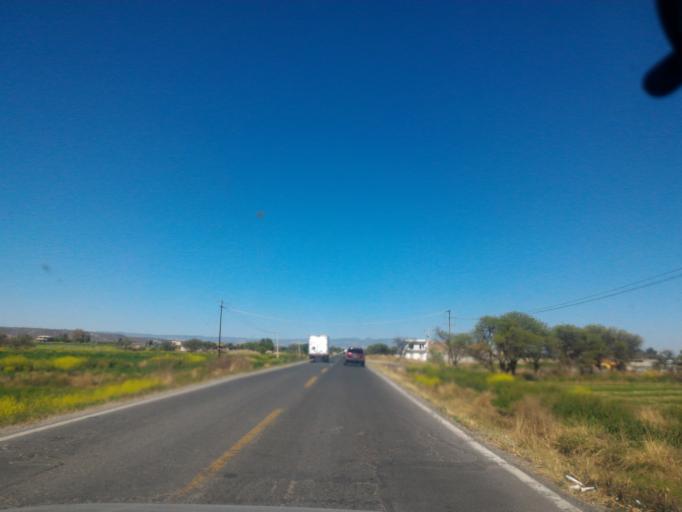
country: MX
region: Guanajuato
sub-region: San Francisco del Rincon
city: San Roque de Montes
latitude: 21.0146
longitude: -101.7974
